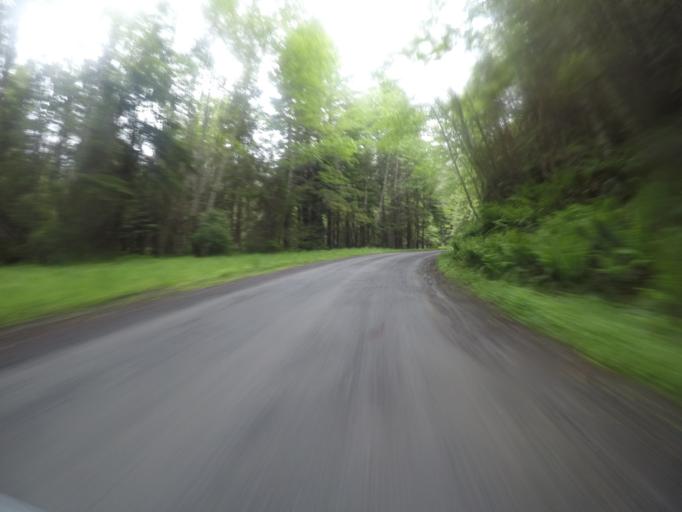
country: US
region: California
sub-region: Humboldt County
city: Westhaven-Moonstone
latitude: 41.2337
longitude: -123.9899
